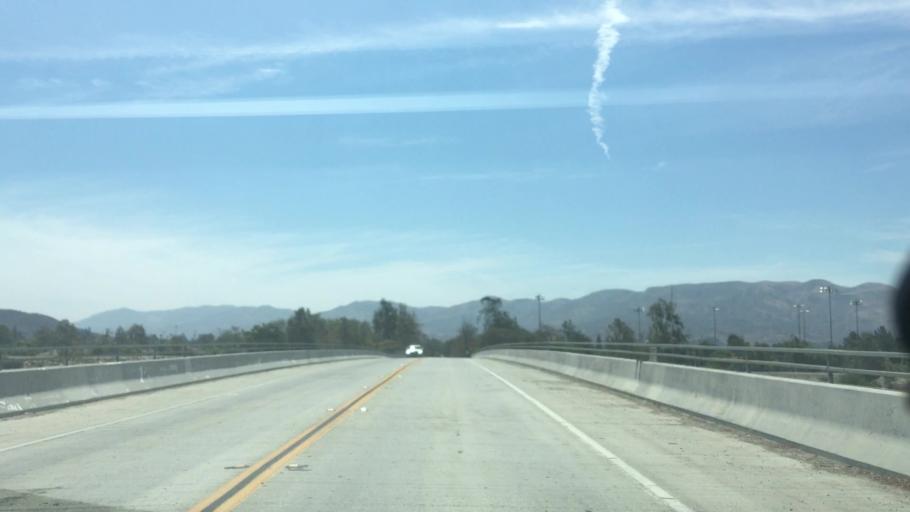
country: US
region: California
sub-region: Ventura County
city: Fillmore
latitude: 34.4062
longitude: -118.9321
